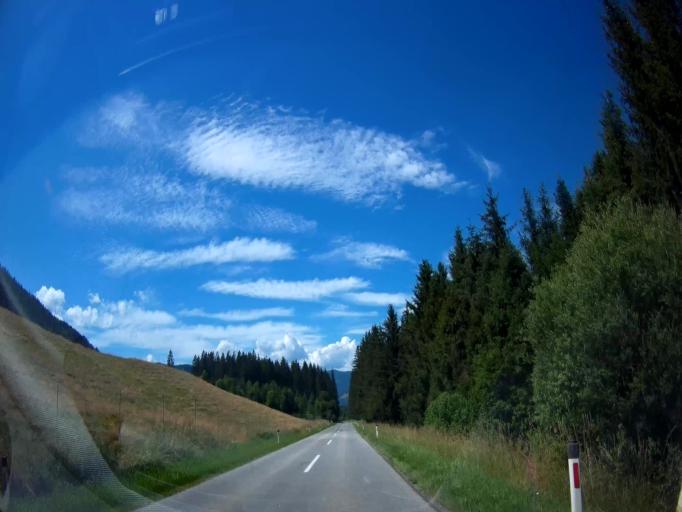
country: AT
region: Carinthia
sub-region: Politischer Bezirk Sankt Veit an der Glan
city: Glodnitz
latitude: 46.8611
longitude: 14.1291
